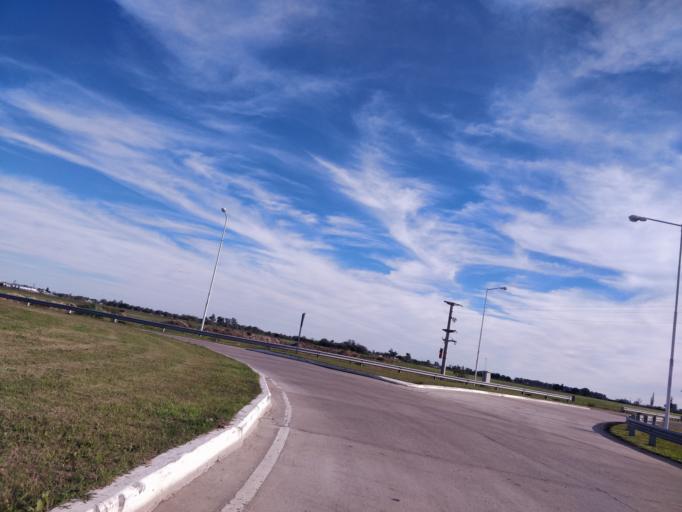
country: AR
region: Cordoba
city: Leones
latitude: -32.6420
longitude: -62.2904
